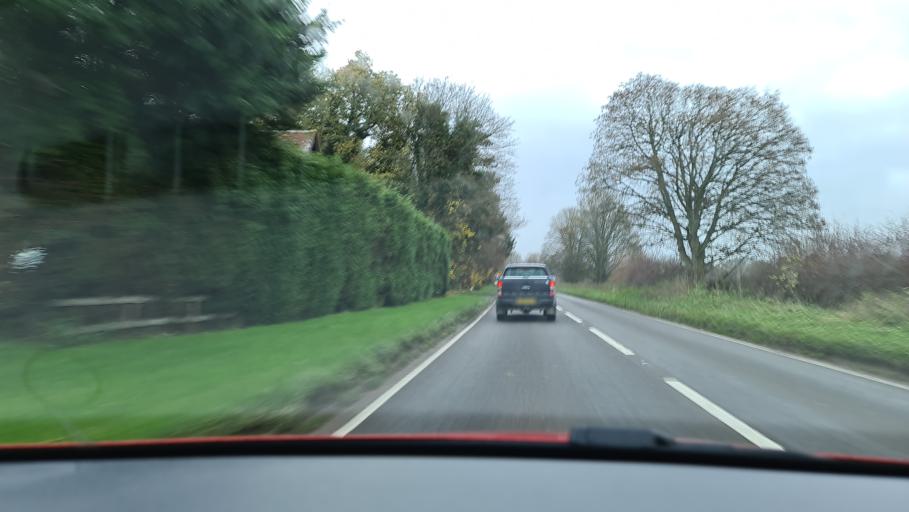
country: GB
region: England
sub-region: Buckinghamshire
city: Great Missenden
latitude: 51.7149
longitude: -0.7154
